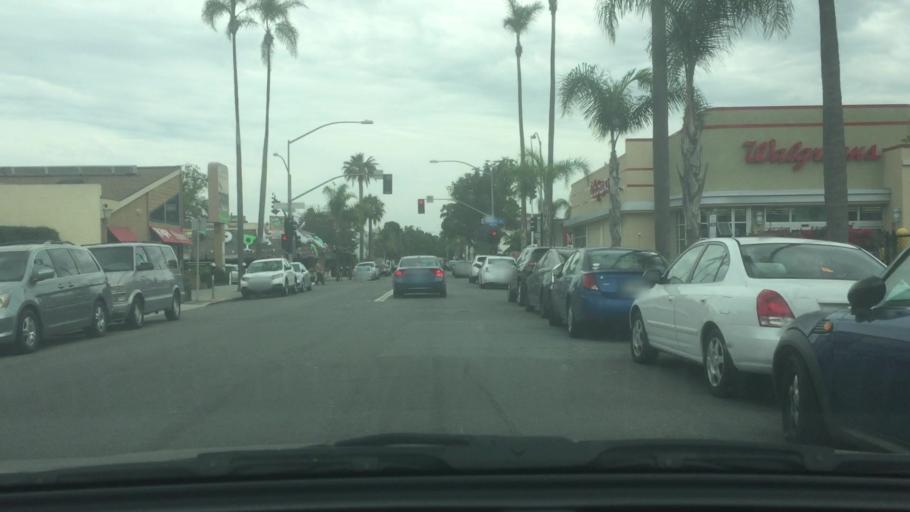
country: US
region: California
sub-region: San Diego County
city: San Diego
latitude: 32.7476
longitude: -117.1627
